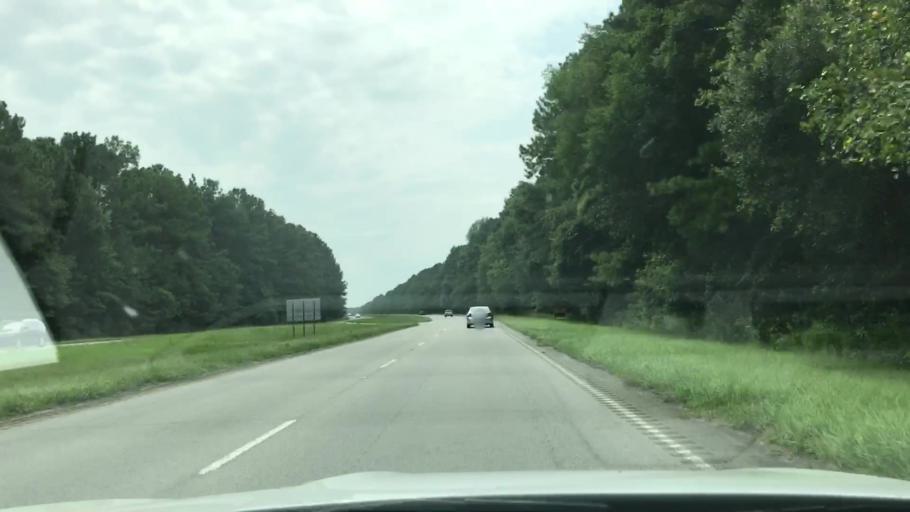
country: US
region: South Carolina
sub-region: Charleston County
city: Awendaw
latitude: 32.9733
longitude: -79.6726
